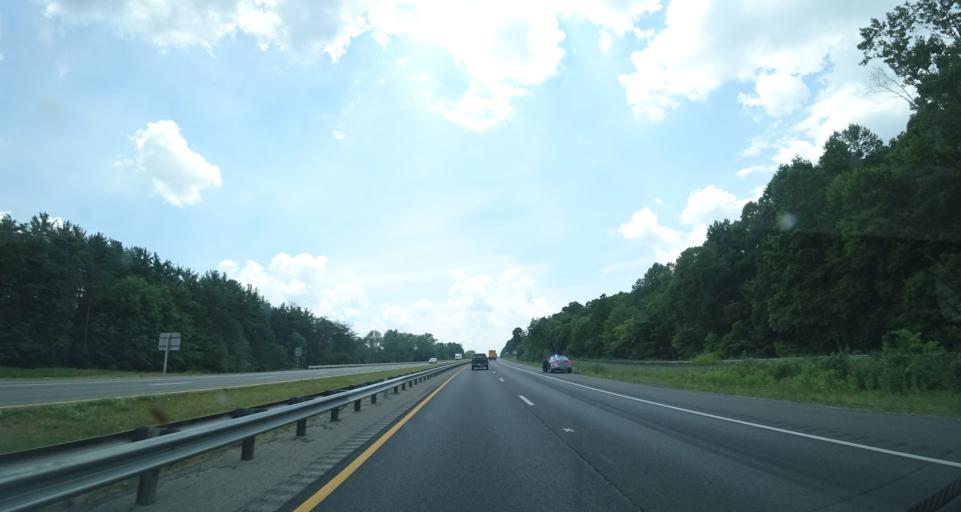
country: US
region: Virginia
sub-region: Pulaski County
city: Pulaski
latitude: 37.0215
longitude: -80.7321
